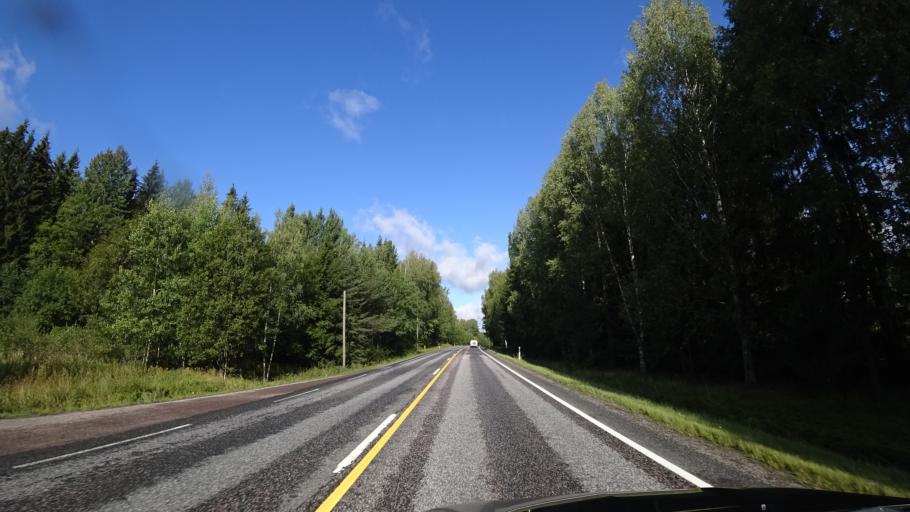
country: FI
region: Uusimaa
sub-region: Helsinki
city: Tuusula
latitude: 60.4462
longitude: 24.9670
